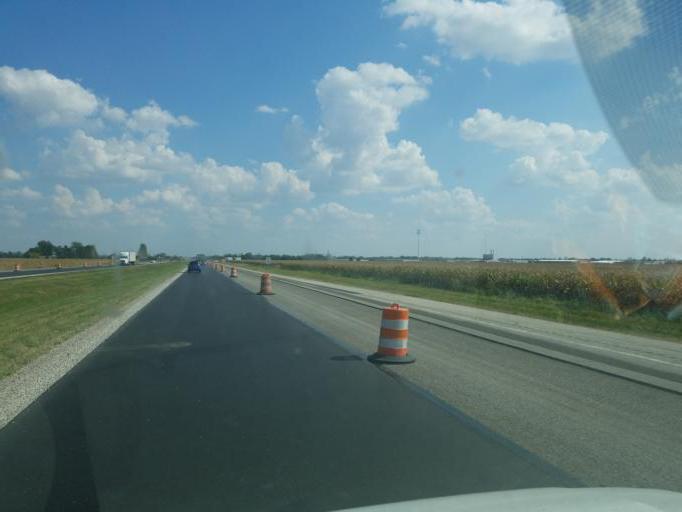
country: US
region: Ohio
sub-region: Van Wert County
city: Van Wert
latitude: 40.8922
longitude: -84.6172
